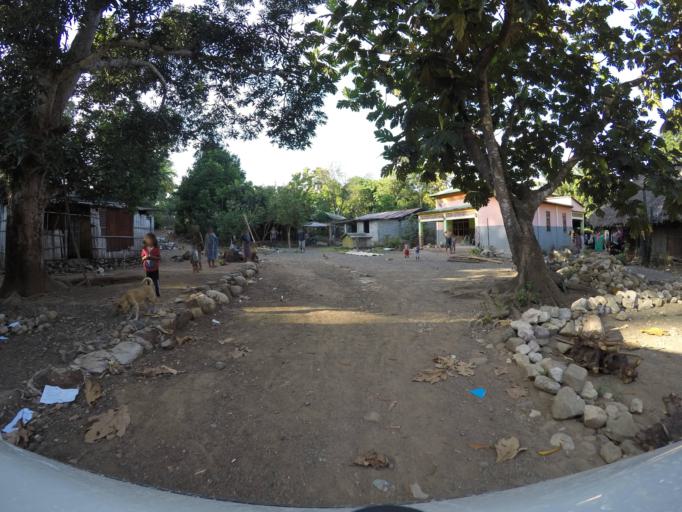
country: TL
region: Viqueque
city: Viqueque
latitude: -8.8327
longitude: 126.3738
